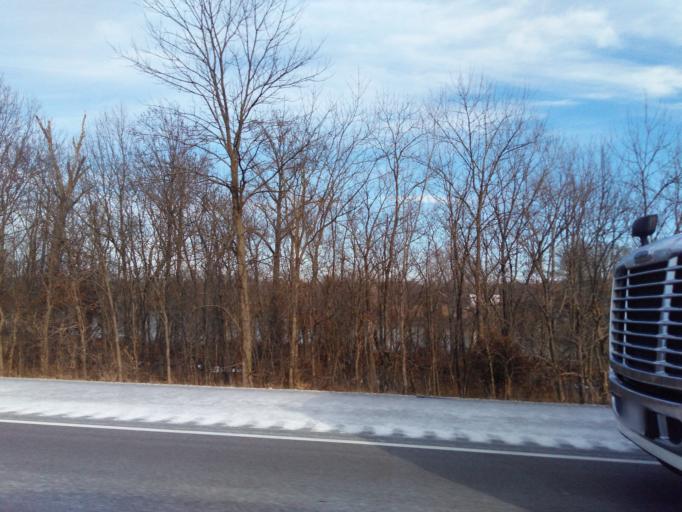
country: US
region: Illinois
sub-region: Jefferson County
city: Ina
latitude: 38.2312
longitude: -88.9058
